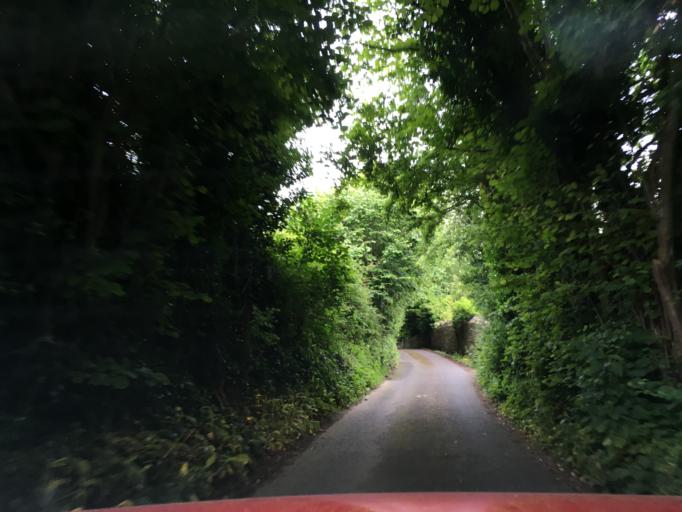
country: GB
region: England
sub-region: North Somerset
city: Dundry
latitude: 51.4040
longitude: -2.6370
